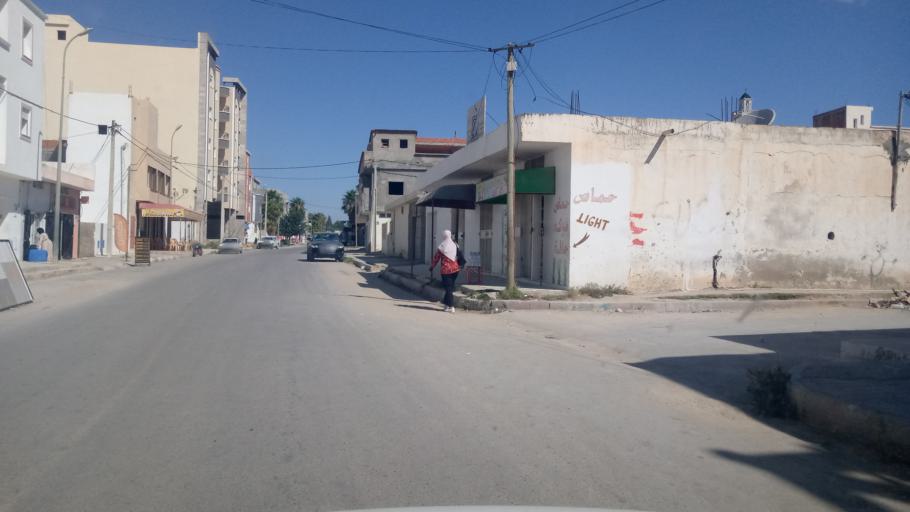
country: TN
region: Al Qayrawan
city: Sbikha
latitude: 36.1174
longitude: 10.0937
